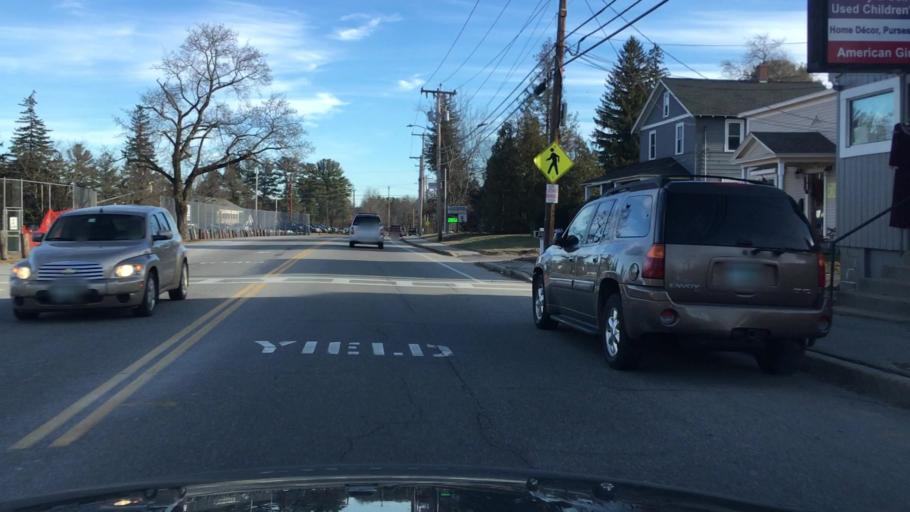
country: US
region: New Hampshire
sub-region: Hillsborough County
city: Milford
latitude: 42.8301
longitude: -71.6366
